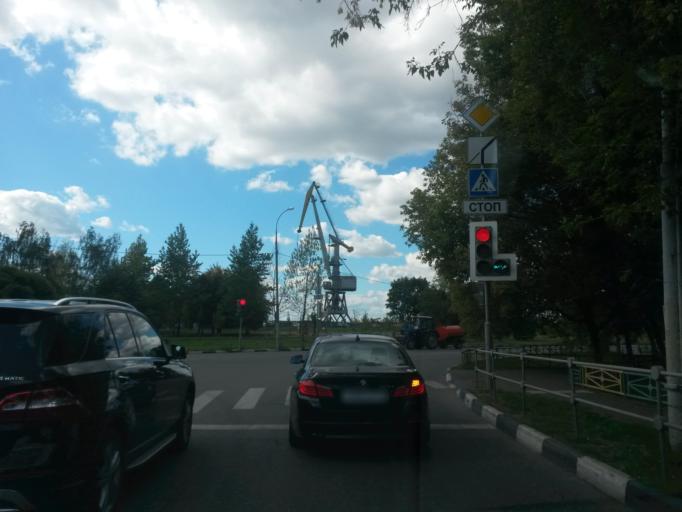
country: RU
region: Moscow
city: Tekstil'shchiki
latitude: 55.6869
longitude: 37.7180
